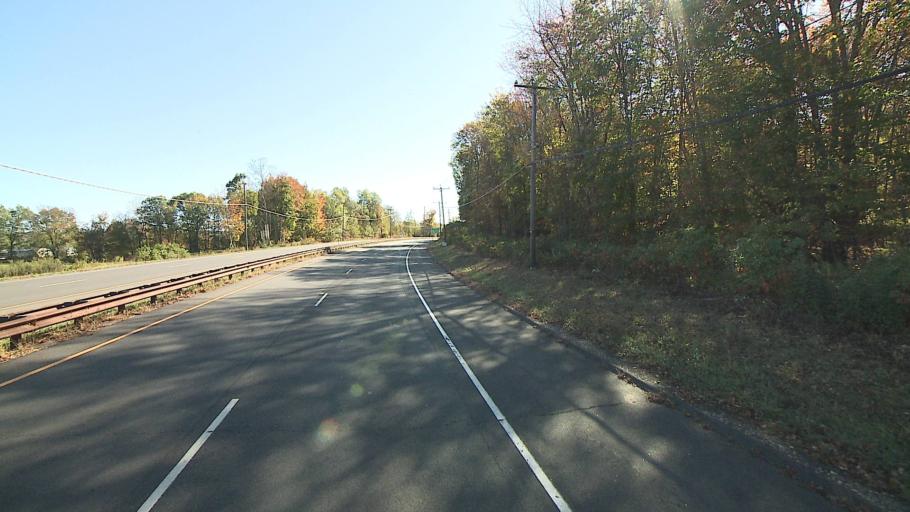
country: US
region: Connecticut
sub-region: Middlesex County
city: Portland
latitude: 41.5754
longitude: -72.6053
